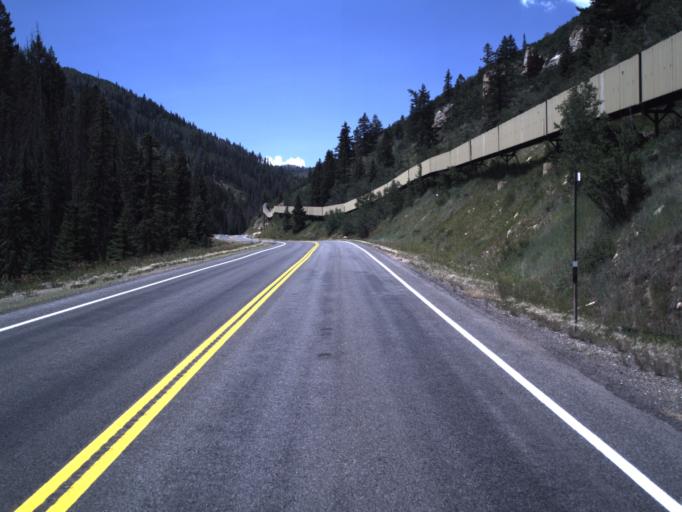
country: US
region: Utah
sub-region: Sanpete County
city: Fairview
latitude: 39.6832
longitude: -111.1704
